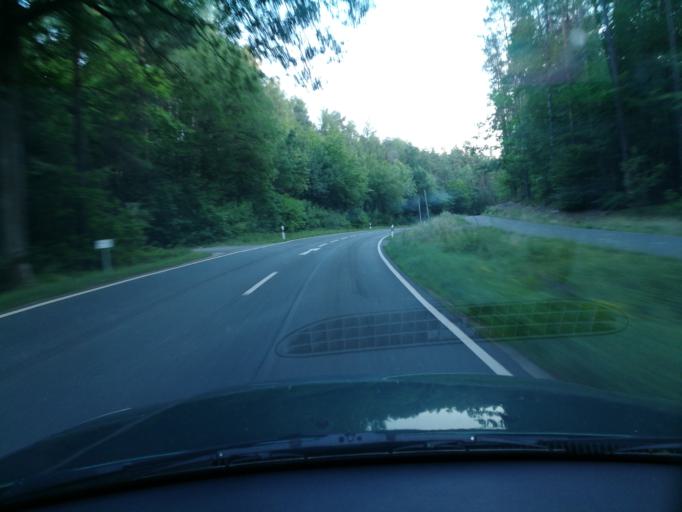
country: DE
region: Bavaria
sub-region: Regierungsbezirk Mittelfranken
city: Hessdorf
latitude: 49.6044
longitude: 10.9017
